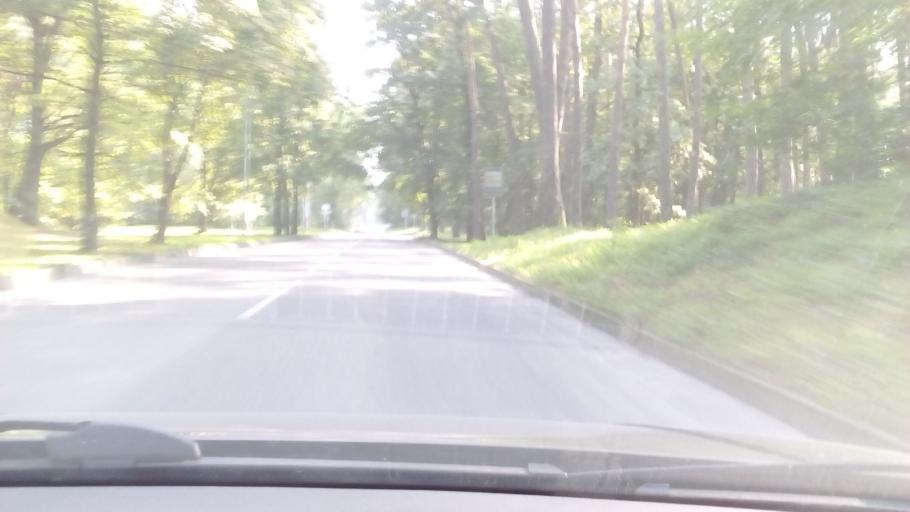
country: LT
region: Alytaus apskritis
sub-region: Alytus
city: Alytus
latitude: 54.3952
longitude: 24.0565
